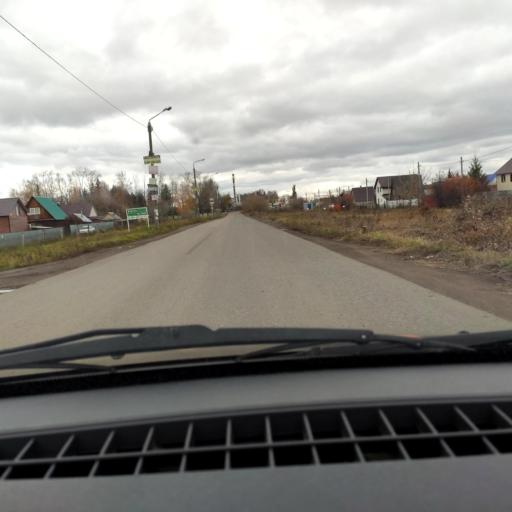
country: RU
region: Bashkortostan
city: Ufa
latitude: 54.5738
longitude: 55.9068
